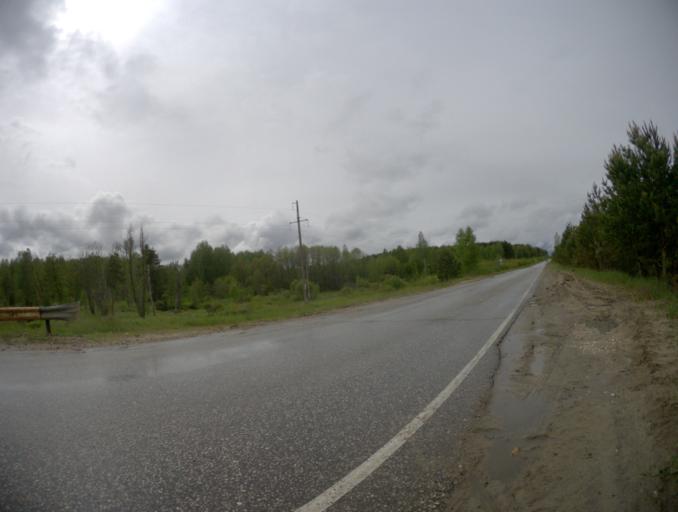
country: RU
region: Vladimir
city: Velikodvorskiy
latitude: 55.3750
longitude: 40.7672
